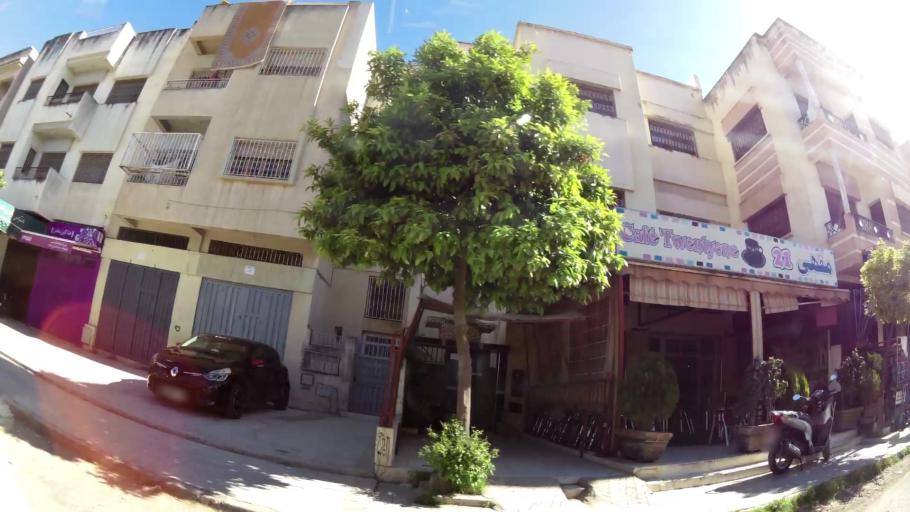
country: MA
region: Fes-Boulemane
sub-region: Fes
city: Fes
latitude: 34.0170
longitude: -4.9732
